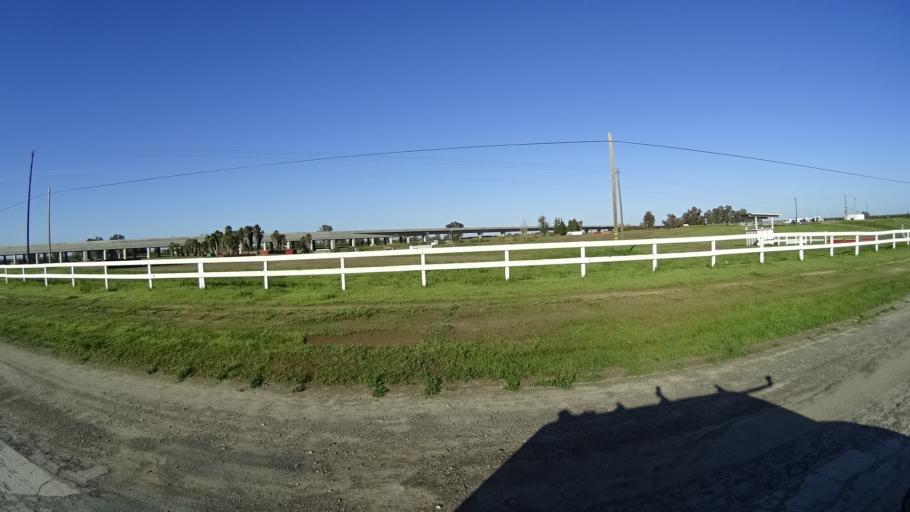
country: US
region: California
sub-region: Fresno County
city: Biola
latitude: 36.8417
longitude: -119.9222
